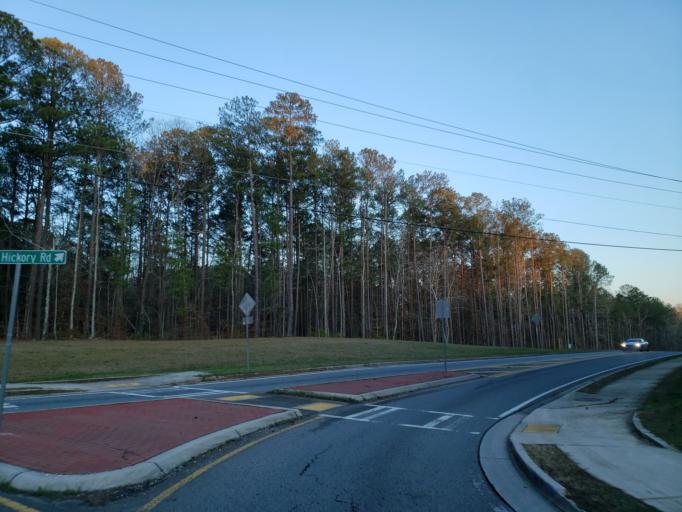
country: US
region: Georgia
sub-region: Cobb County
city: Acworth
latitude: 33.9982
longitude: -84.7290
